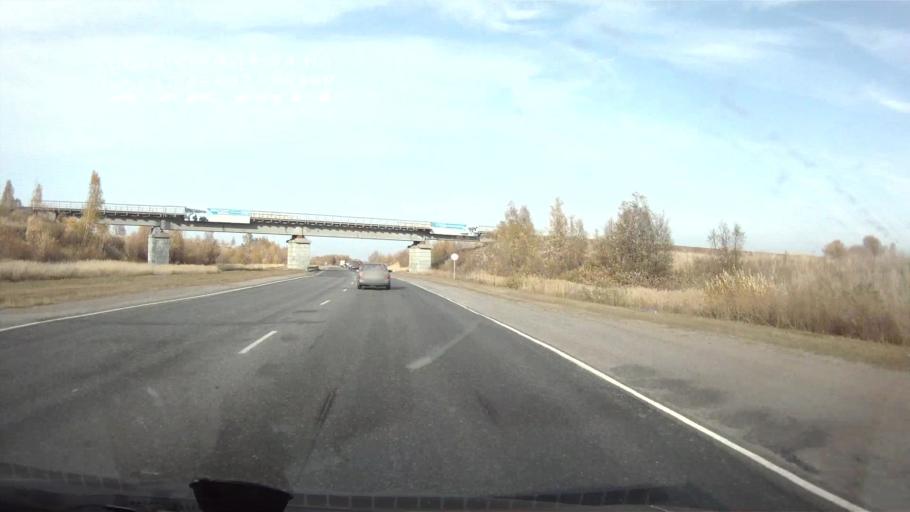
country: RU
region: Chuvashia
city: Kugesi
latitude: 56.0408
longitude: 47.3652
